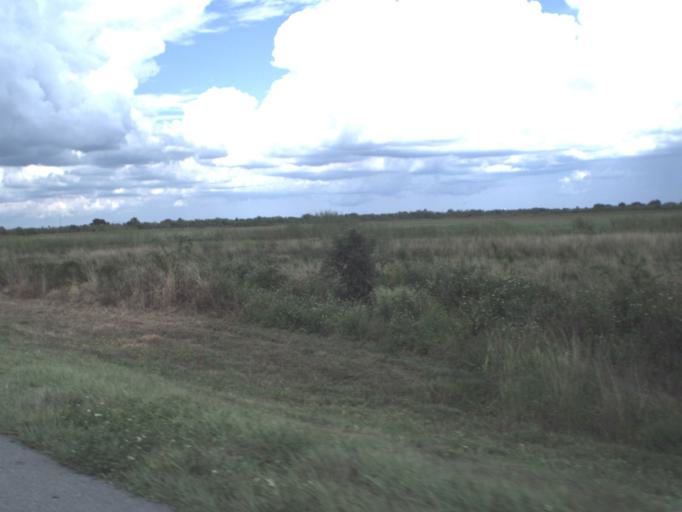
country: US
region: Florida
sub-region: Okeechobee County
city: Okeechobee
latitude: 27.1827
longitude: -80.8532
